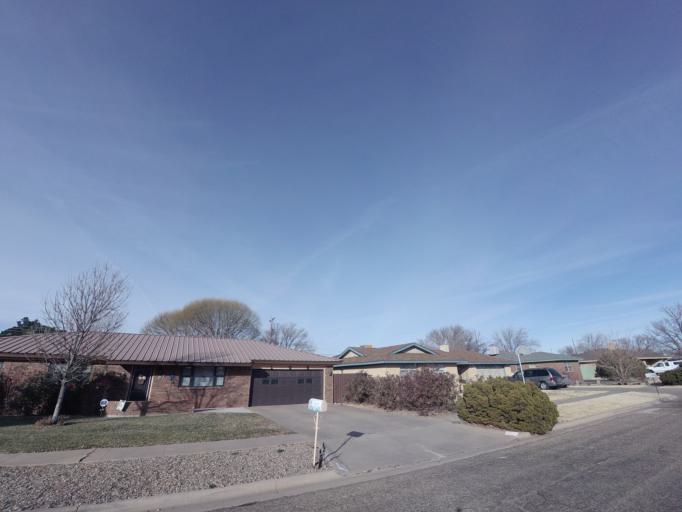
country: US
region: New Mexico
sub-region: Curry County
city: Clovis
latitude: 34.4165
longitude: -103.2239
